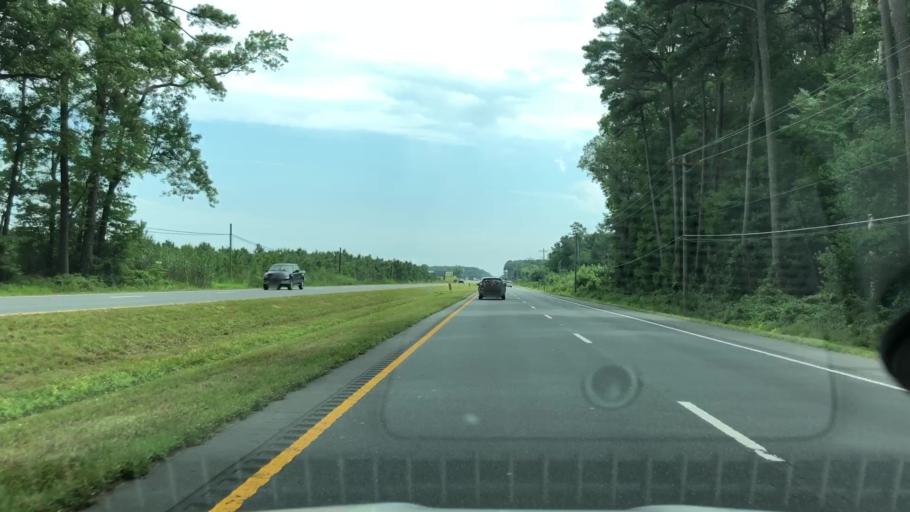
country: US
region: Virginia
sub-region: Accomack County
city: Wattsville
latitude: 37.9200
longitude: -75.5495
